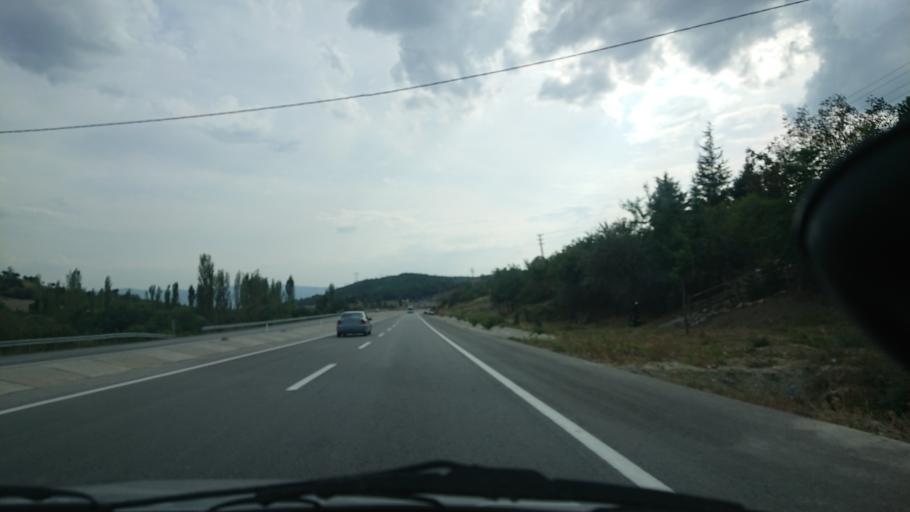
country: TR
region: Kuetahya
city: Gediz
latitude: 39.0379
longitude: 29.4216
